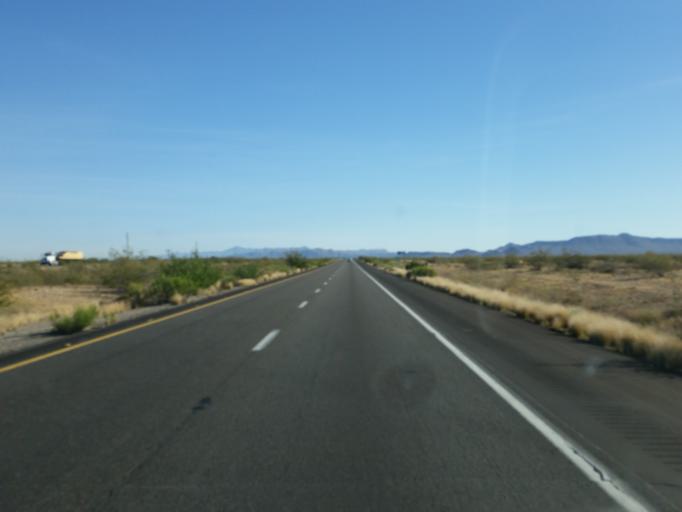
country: US
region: Arizona
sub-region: Mohave County
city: Kingman
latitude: 34.9889
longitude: -114.1385
